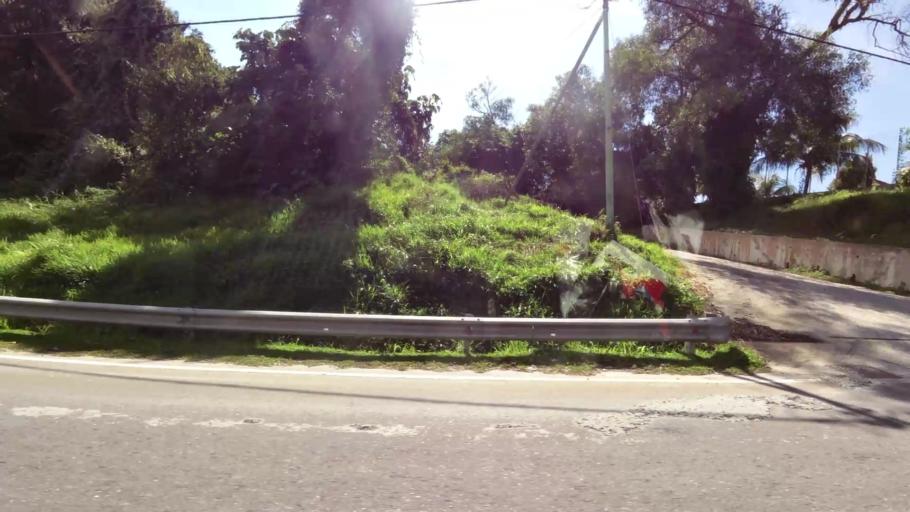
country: BN
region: Brunei and Muara
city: Bandar Seri Begawan
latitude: 4.9595
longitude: 114.9440
